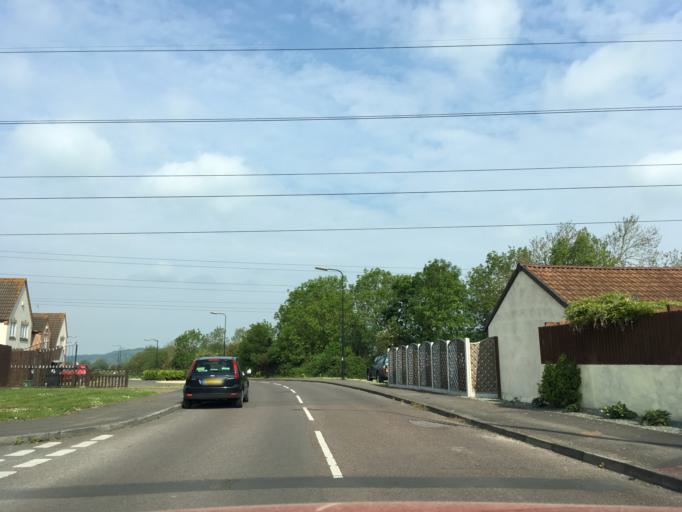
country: GB
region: England
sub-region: North Somerset
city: Nailsea
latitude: 51.4311
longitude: -2.7784
